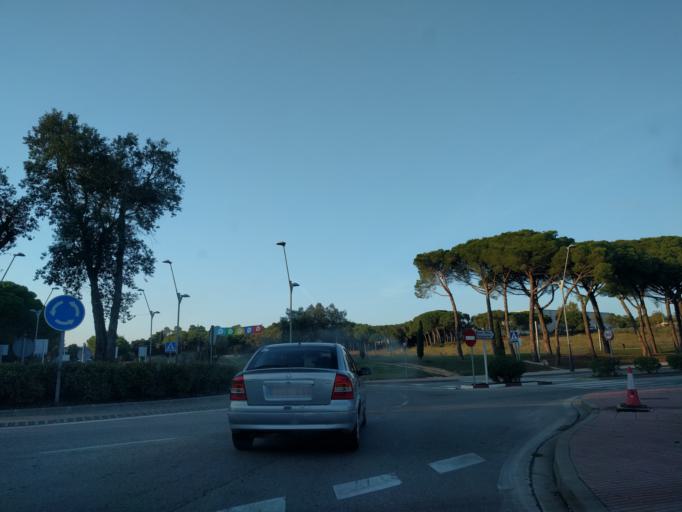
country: ES
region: Catalonia
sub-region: Provincia de Girona
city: Sant Feliu de Guixols
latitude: 41.7953
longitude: 3.0197
